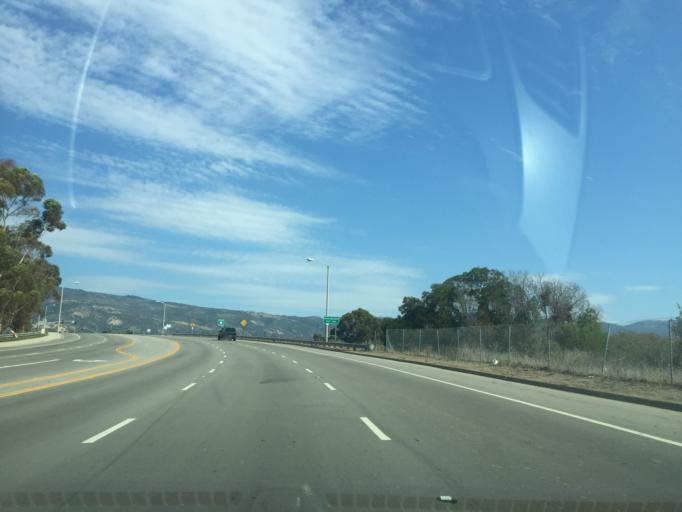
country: US
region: California
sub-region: Santa Barbara County
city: Isla Vista
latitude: 34.4345
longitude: -119.8533
